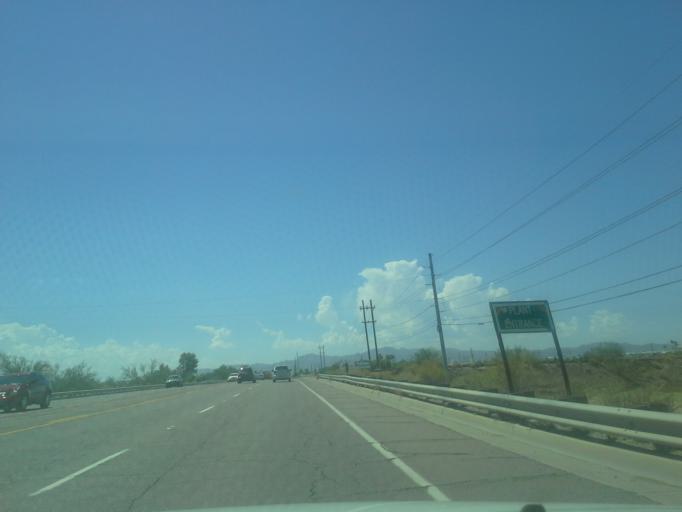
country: US
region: Arizona
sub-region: Maricopa County
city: Youngtown
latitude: 33.5366
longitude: -112.3165
